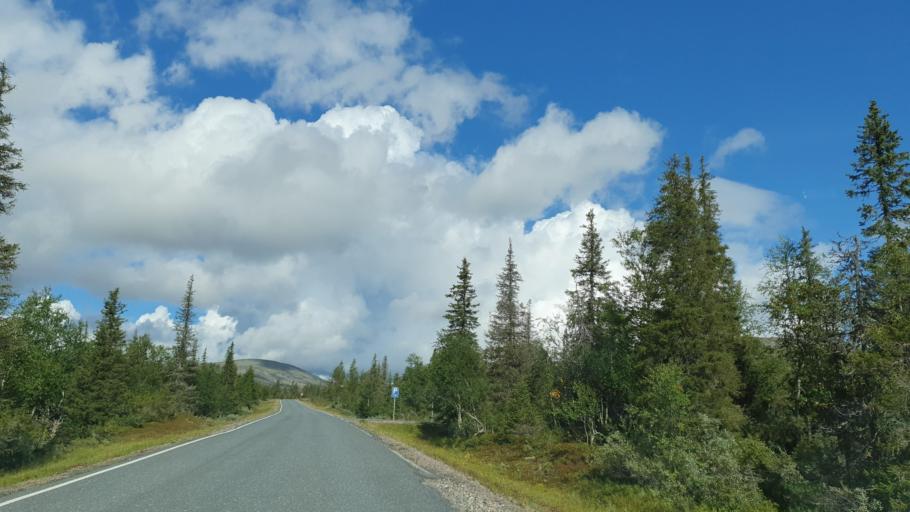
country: FI
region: Lapland
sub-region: Tunturi-Lappi
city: Muonio
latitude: 68.0412
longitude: 24.0675
